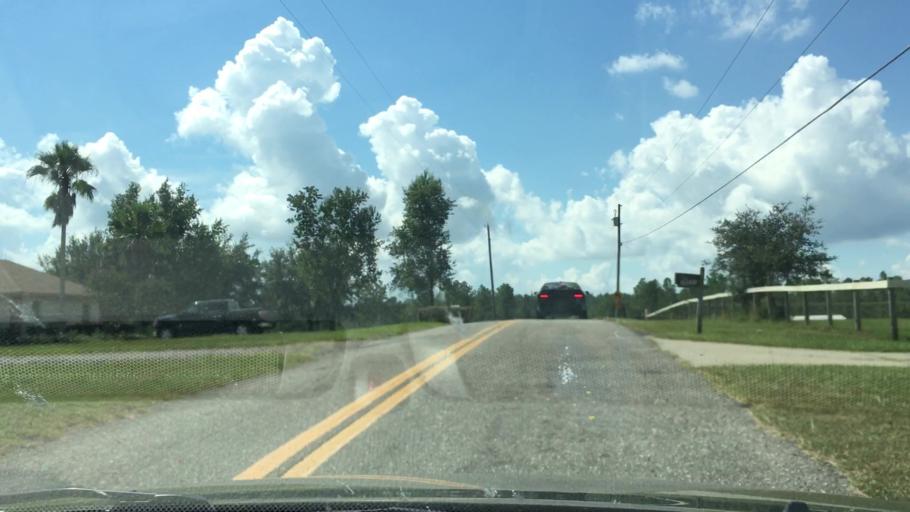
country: US
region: Florida
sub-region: Lake County
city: Minneola
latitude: 28.6393
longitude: -81.7311
